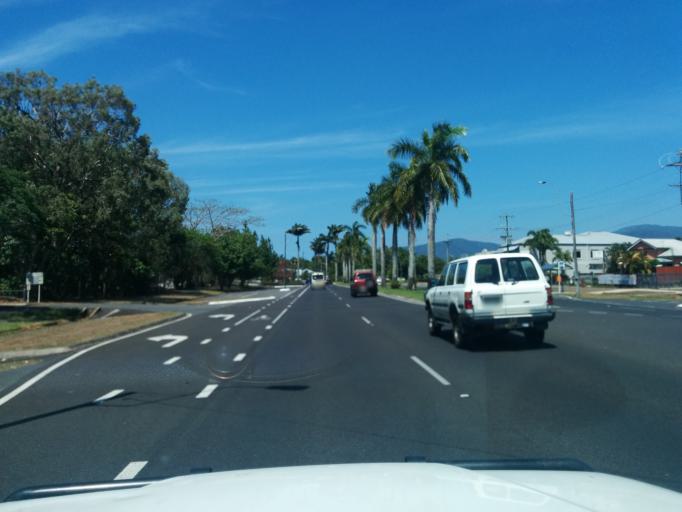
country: AU
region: Queensland
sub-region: Cairns
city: Cairns
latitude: -16.9135
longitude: 145.7528
